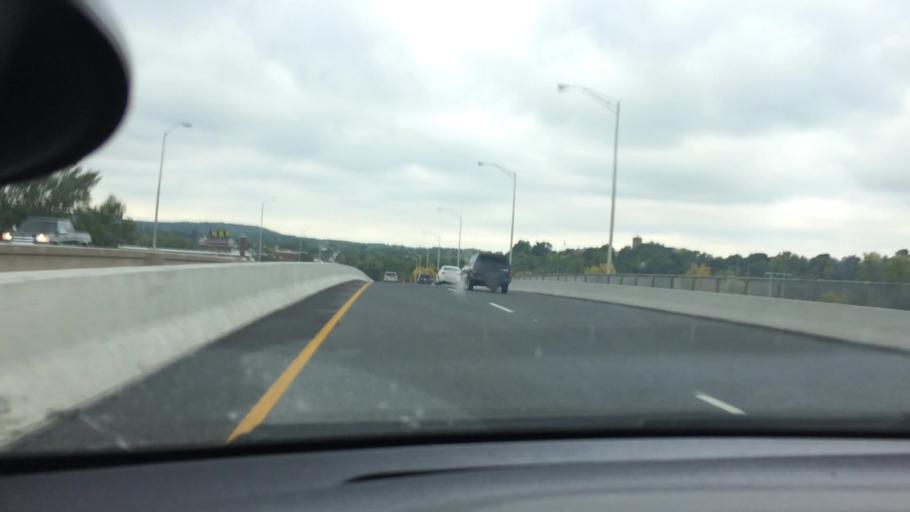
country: US
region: Wisconsin
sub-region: Chippewa County
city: Chippewa Falls
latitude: 44.9295
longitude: -91.3860
